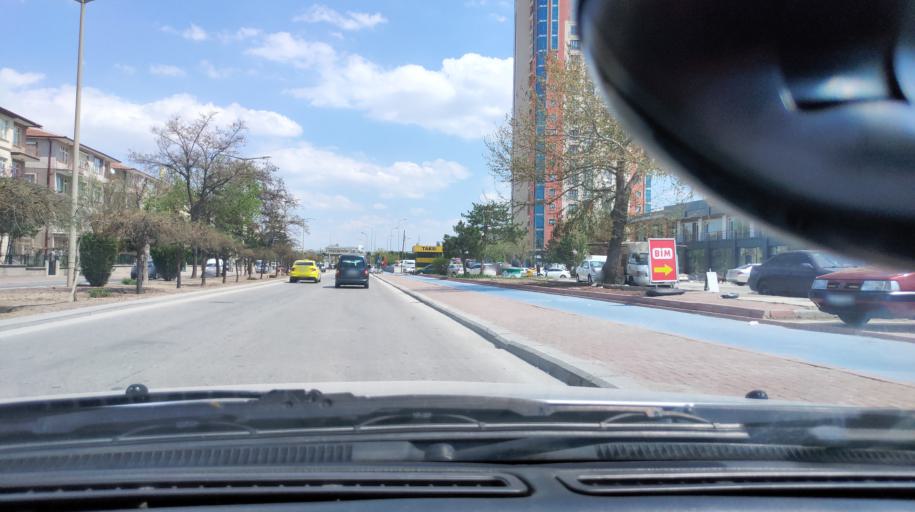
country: TR
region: Konya
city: Selcuklu
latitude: 37.9287
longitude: 32.5058
